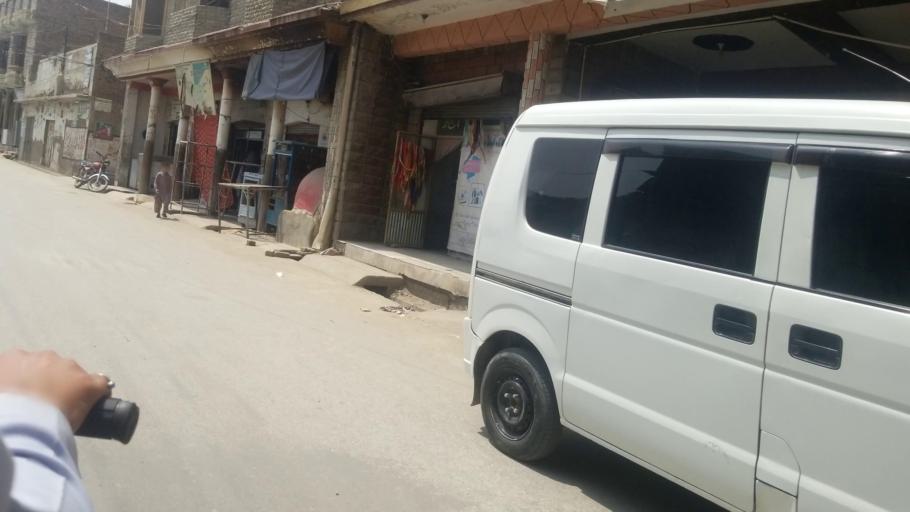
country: PK
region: Khyber Pakhtunkhwa
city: Peshawar
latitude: 34.0279
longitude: 71.5886
